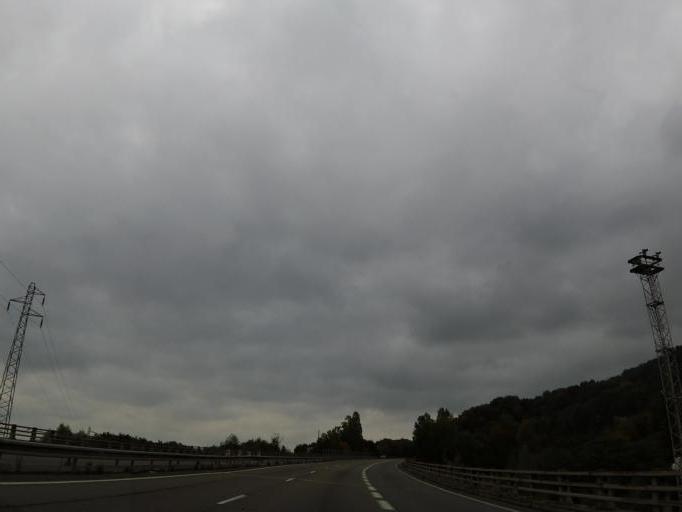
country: FR
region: Lorraine
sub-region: Departement de la Moselle
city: Cocheren
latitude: 49.1609
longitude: 6.8558
